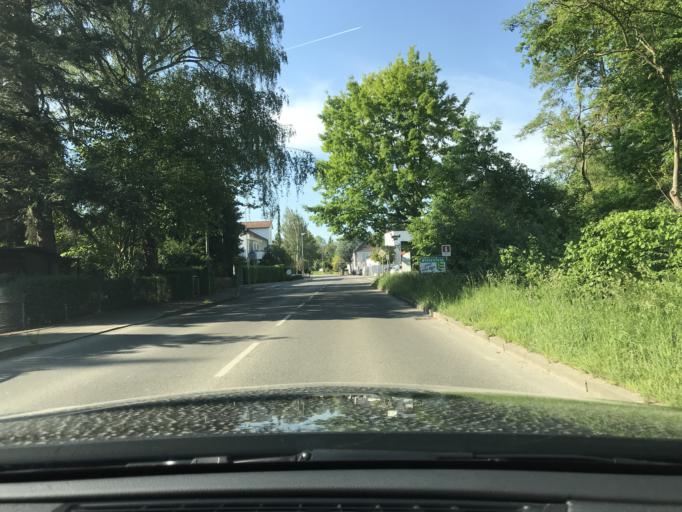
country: DE
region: Baden-Wuerttemberg
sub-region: Regierungsbezirk Stuttgart
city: Schwaikheim
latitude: 48.8842
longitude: 9.3154
